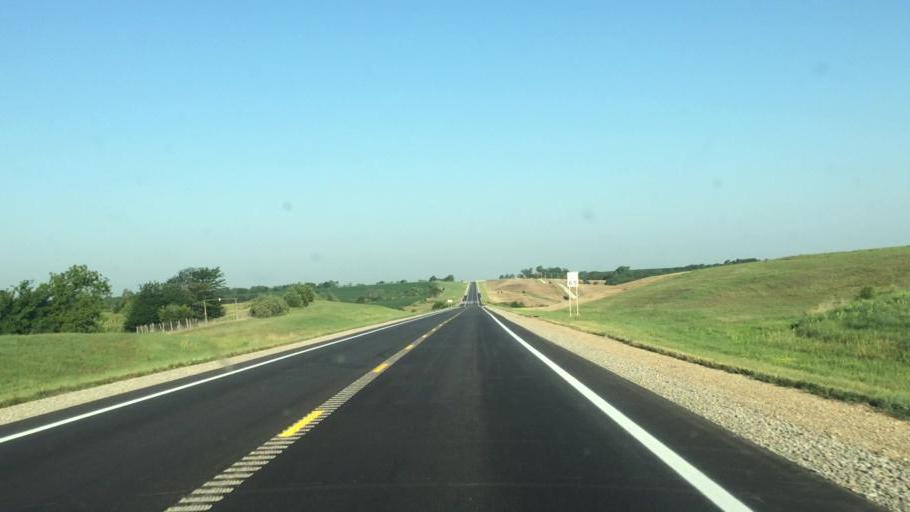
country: US
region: Kansas
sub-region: Doniphan County
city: Highland
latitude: 39.8412
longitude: -95.3712
